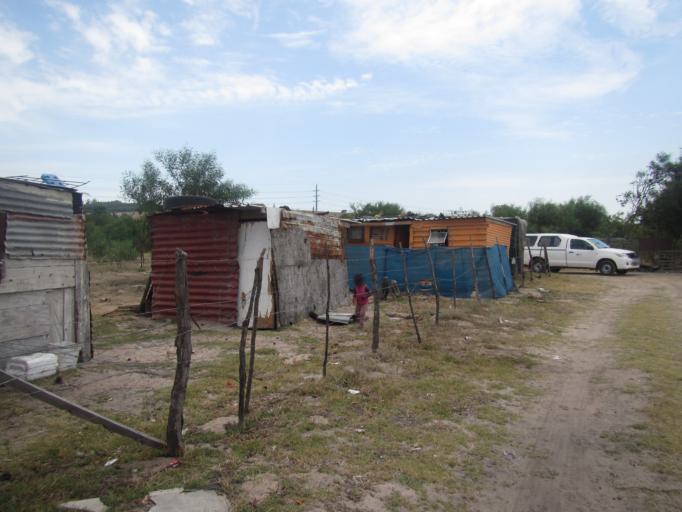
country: ZA
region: Western Cape
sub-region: Cape Winelands District Municipality
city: Stellenbosch
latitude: -33.8049
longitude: 18.8562
